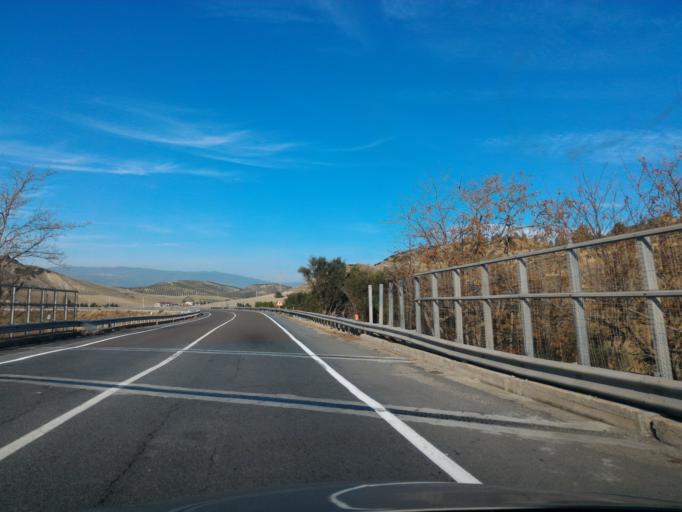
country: IT
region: Calabria
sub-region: Provincia di Crotone
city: Le Castella
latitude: 38.9455
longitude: 16.9529
